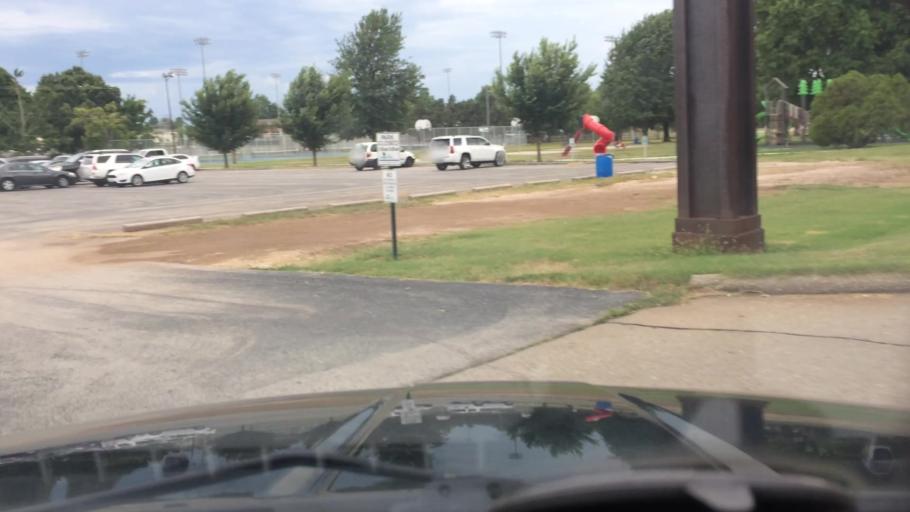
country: US
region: Missouri
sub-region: Greene County
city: Springfield
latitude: 37.1670
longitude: -93.2683
